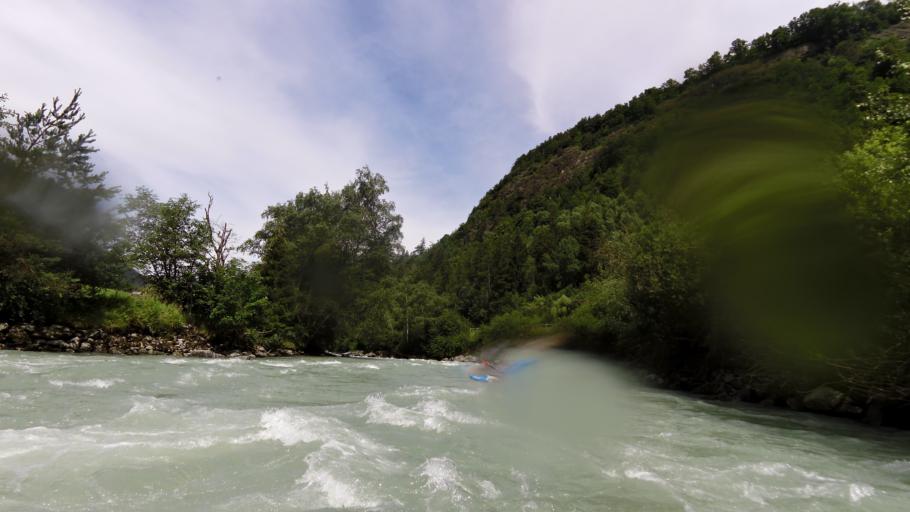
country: AT
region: Tyrol
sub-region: Politischer Bezirk Imst
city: Sautens
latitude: 47.2064
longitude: 10.8788
